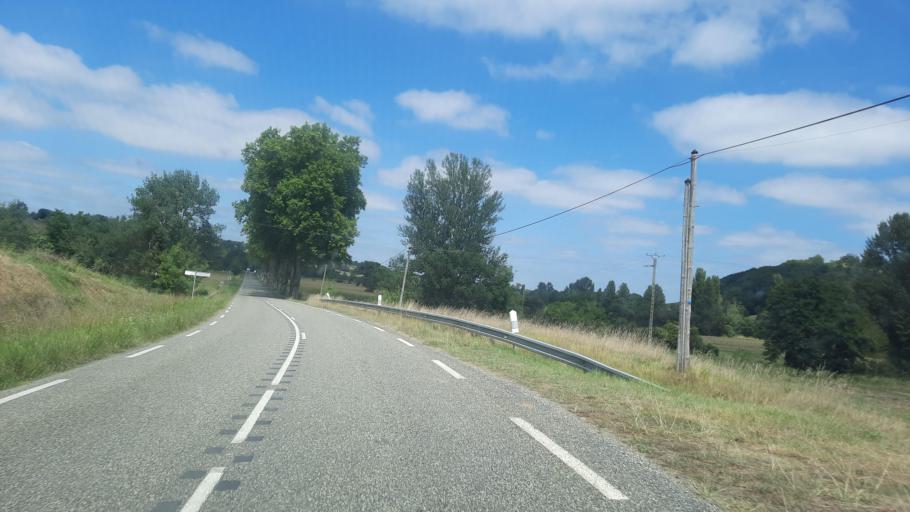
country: FR
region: Midi-Pyrenees
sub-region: Departement de la Haute-Garonne
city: Boulogne-sur-Gesse
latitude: 43.3701
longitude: 0.7528
